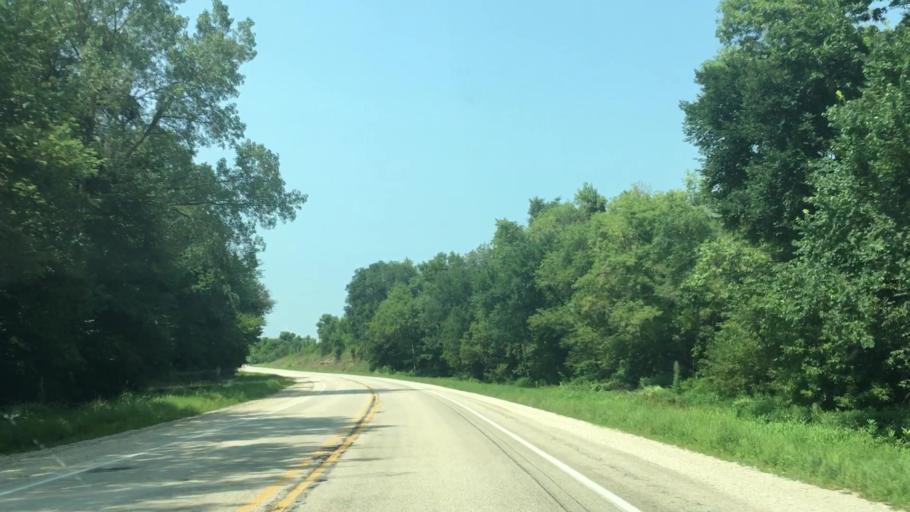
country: US
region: Iowa
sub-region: Fayette County
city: West Union
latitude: 43.0778
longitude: -91.8400
